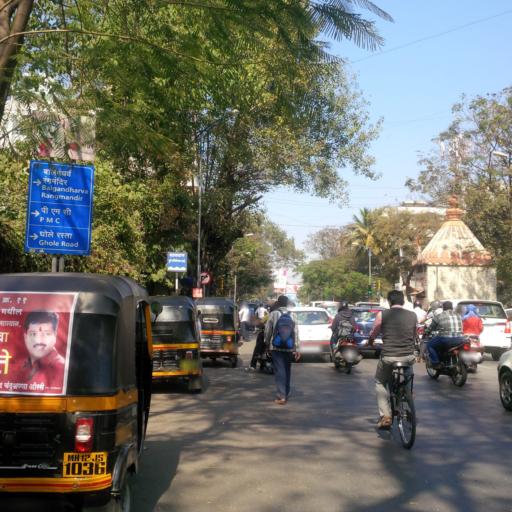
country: IN
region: Maharashtra
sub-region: Pune Division
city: Shivaji Nagar
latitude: 18.5241
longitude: 73.8412
